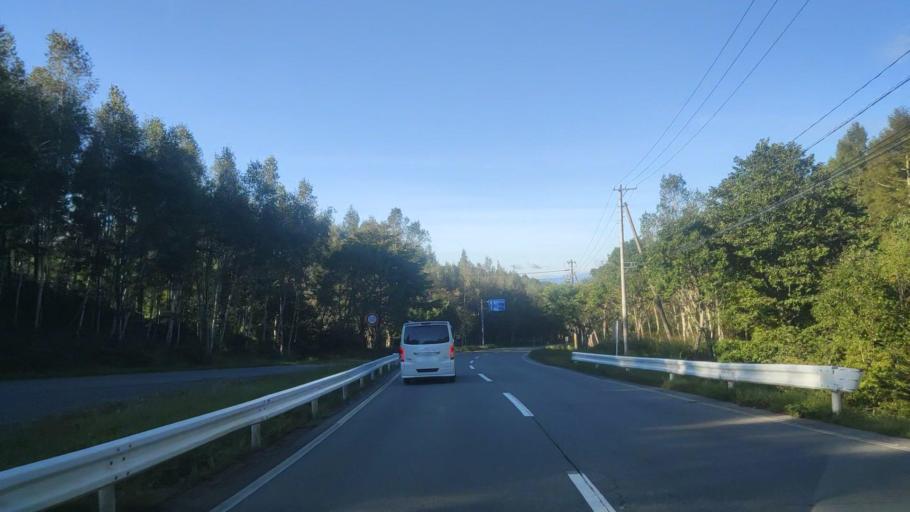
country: JP
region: Nagano
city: Kamimaruko
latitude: 36.1847
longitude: 138.2846
